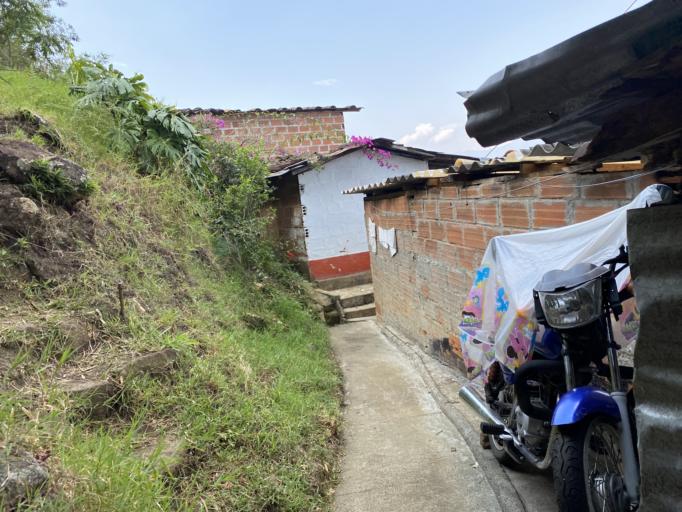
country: CO
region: Antioquia
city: Medellin
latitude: 6.2812
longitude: -75.5435
